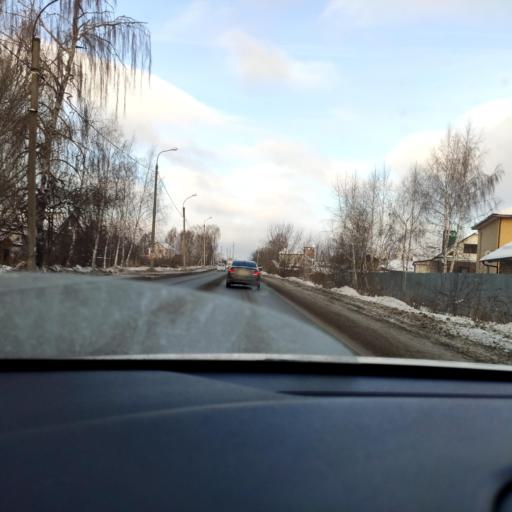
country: RU
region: Tatarstan
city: Osinovo
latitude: 55.8460
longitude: 48.8926
